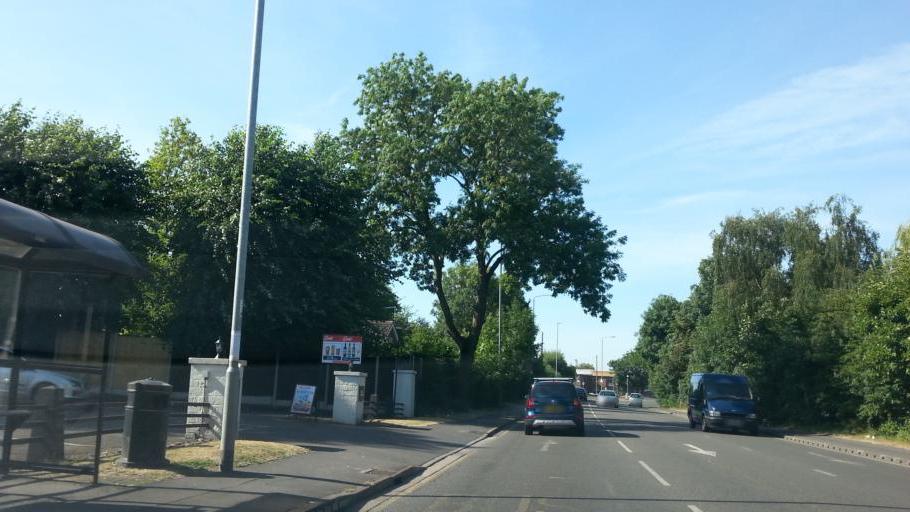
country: GB
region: England
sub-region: Derbyshire
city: Long Eaton
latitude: 52.9073
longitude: -1.2361
